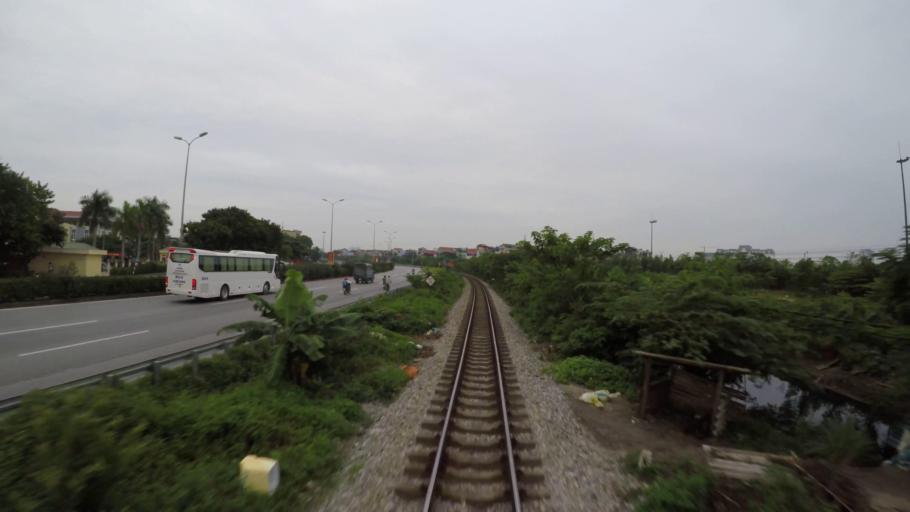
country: VN
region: Ha Noi
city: Trau Quy
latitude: 21.0093
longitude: 105.9544
